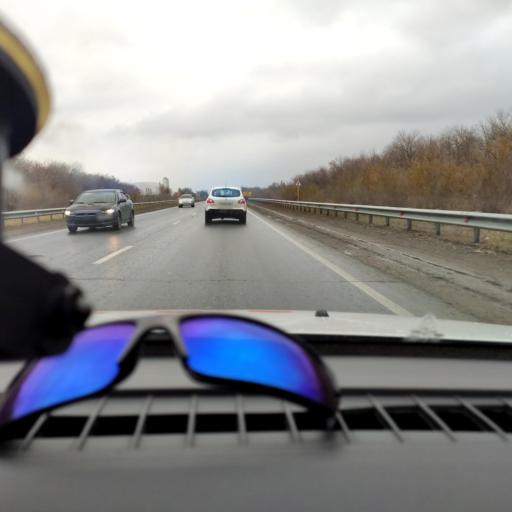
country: RU
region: Samara
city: Samara
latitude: 53.0809
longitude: 50.1070
